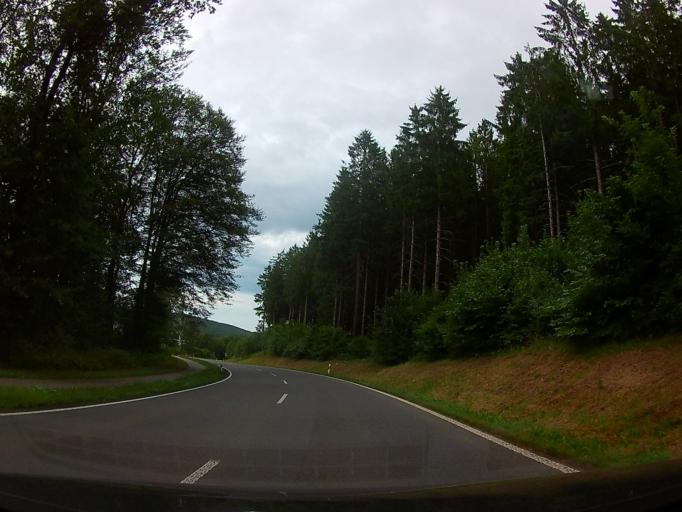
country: DE
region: North Rhine-Westphalia
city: Meinerzhagen
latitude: 51.0999
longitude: 7.6677
